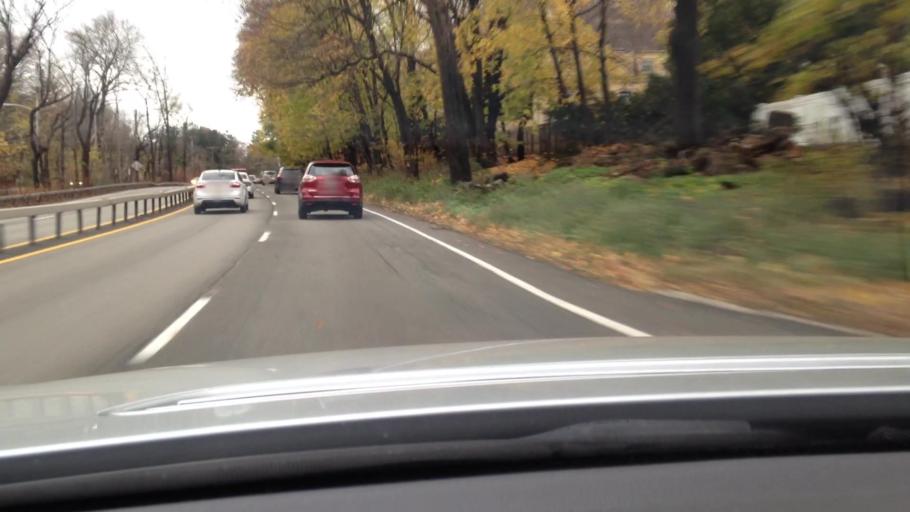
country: US
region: New York
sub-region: Westchester County
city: Briarcliff Manor
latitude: 41.1547
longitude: -73.8333
